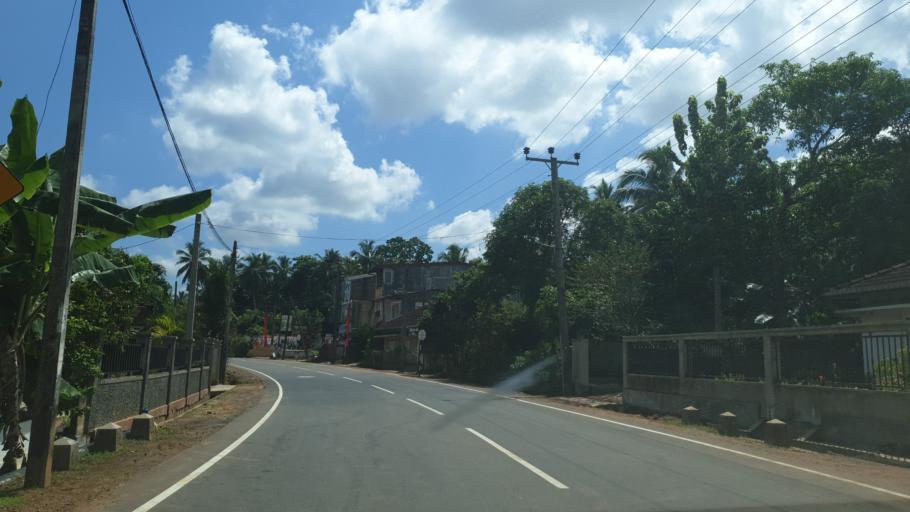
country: LK
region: Western
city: Kalutara
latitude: 6.6639
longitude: 79.9695
